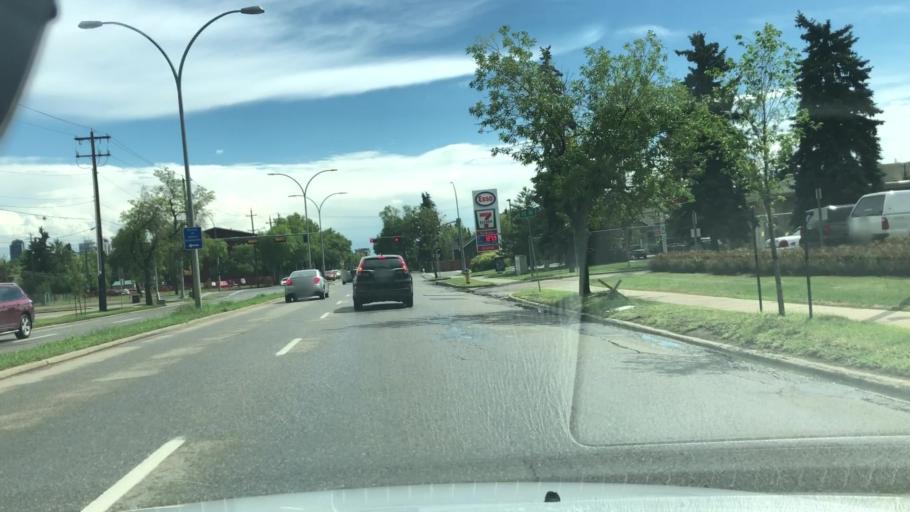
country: CA
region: Alberta
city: Edmonton
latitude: 53.5600
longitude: -113.5085
